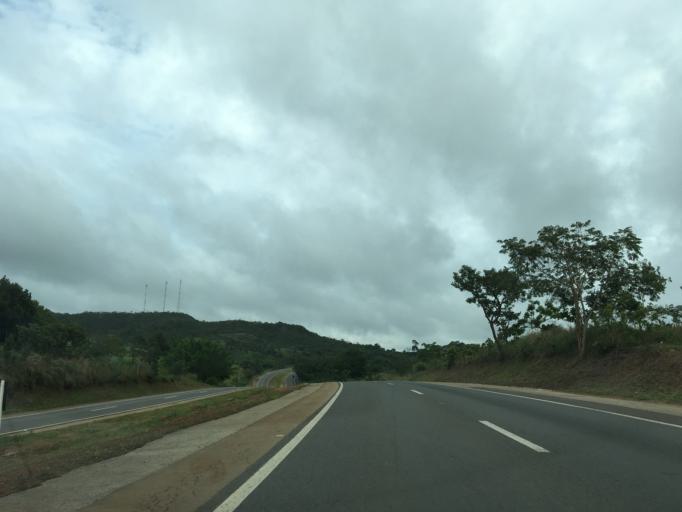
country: BR
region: Goias
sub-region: Luziania
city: Luziania
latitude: -16.1135
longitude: -48.3100
